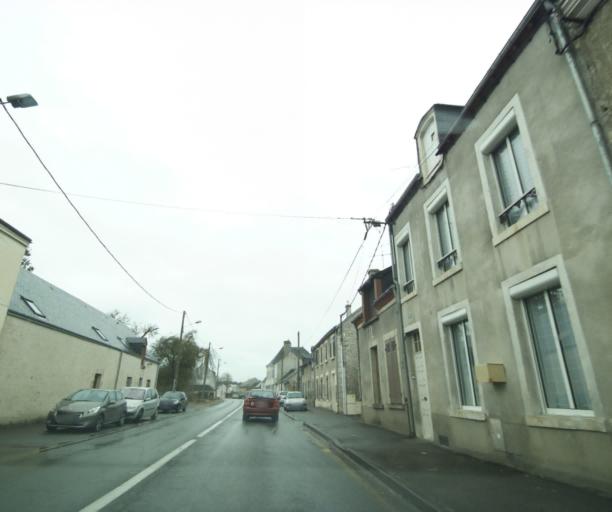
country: FR
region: Centre
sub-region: Departement du Loiret
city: Chevilly
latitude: 48.0250
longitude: 1.8744
